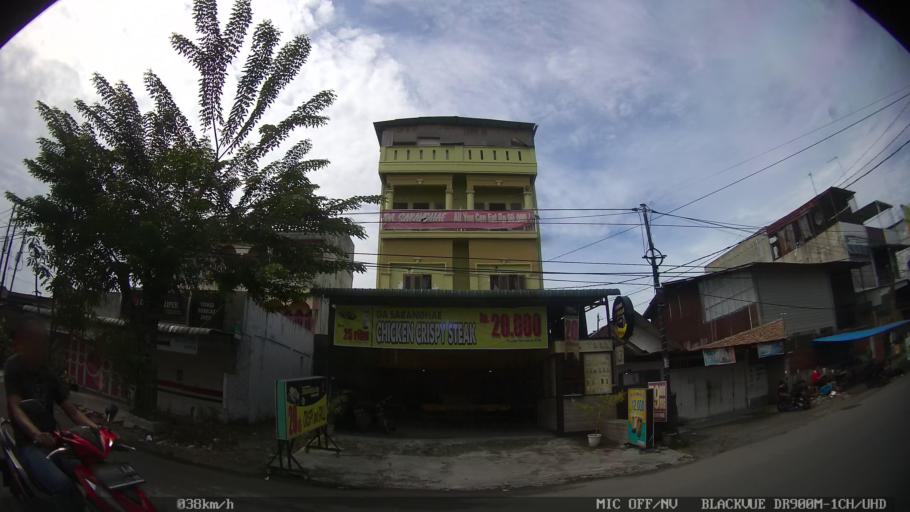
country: ID
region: North Sumatra
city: Medan
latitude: 3.6225
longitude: 98.6852
